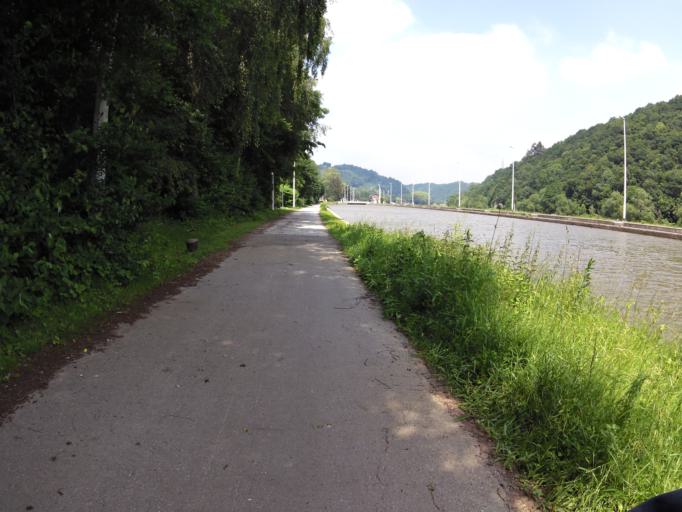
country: BE
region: Wallonia
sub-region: Province de Namur
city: Hastiere-Lavaux
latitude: 50.2006
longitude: 4.8184
